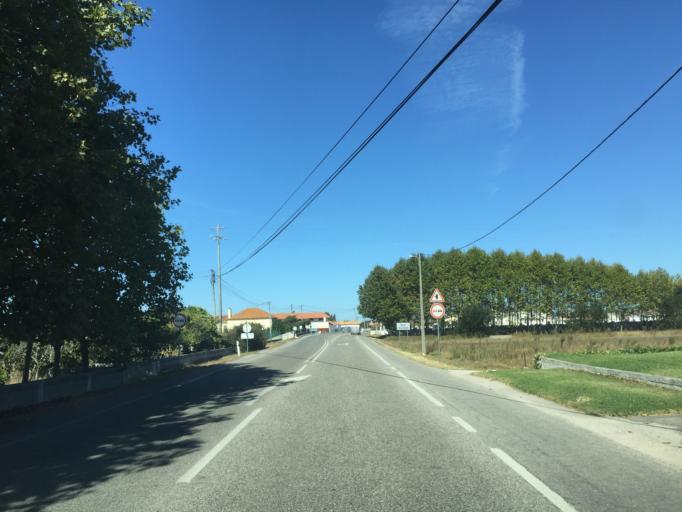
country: PT
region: Coimbra
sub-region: Figueira da Foz
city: Alhadas
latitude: 40.2643
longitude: -8.7797
